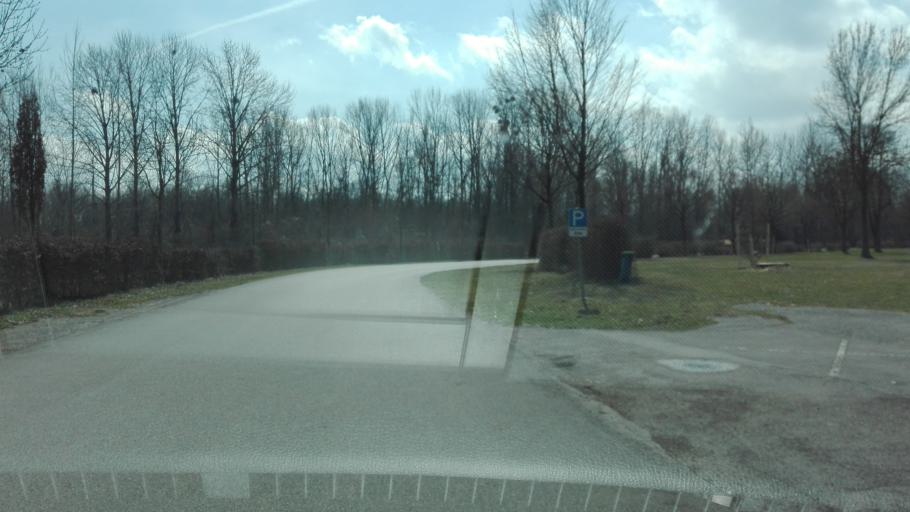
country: AT
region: Upper Austria
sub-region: Politischer Bezirk Urfahr-Umgebung
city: Goldworth
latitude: 48.3241
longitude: 14.0750
